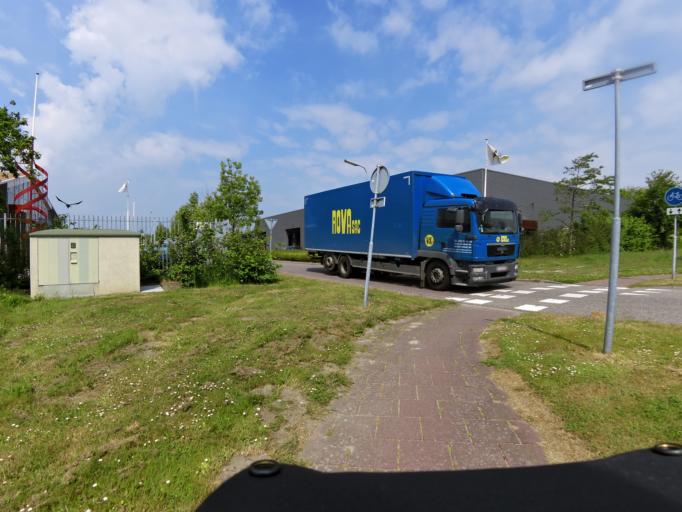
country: NL
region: Zeeland
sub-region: Schouwen-Duiveland
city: Scharendijke
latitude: 51.6415
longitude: 3.9248
